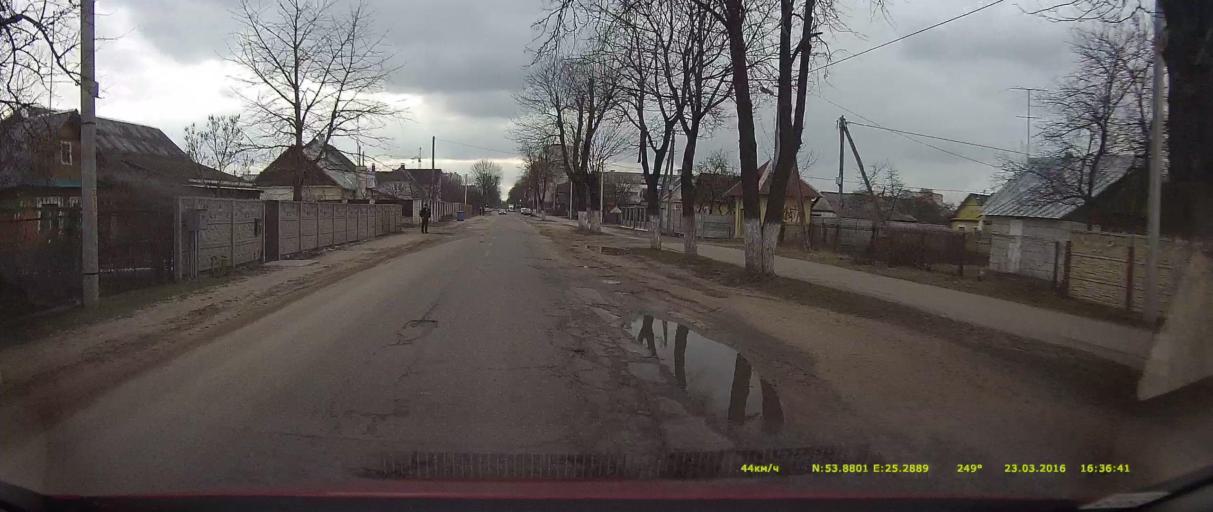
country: BY
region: Grodnenskaya
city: Lida
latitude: 53.8801
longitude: 25.2889
